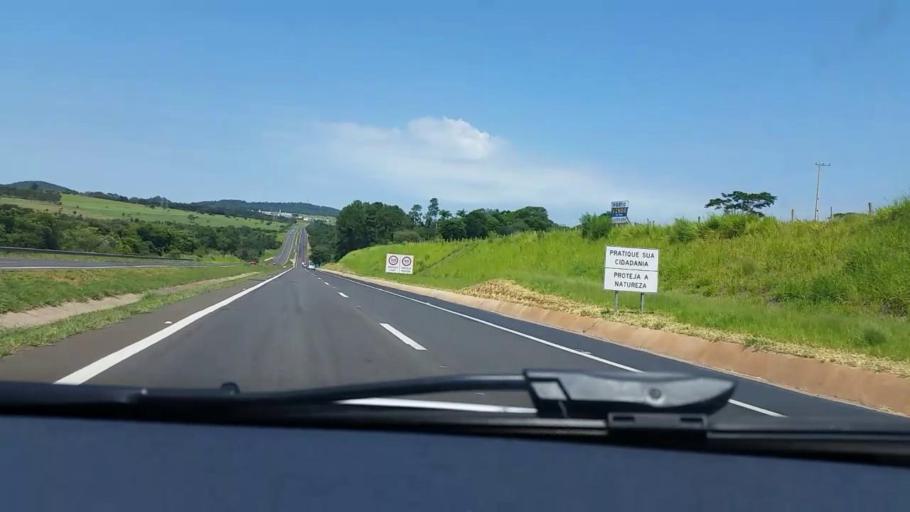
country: BR
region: Sao Paulo
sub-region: Bauru
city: Bauru
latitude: -22.4025
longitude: -49.0927
